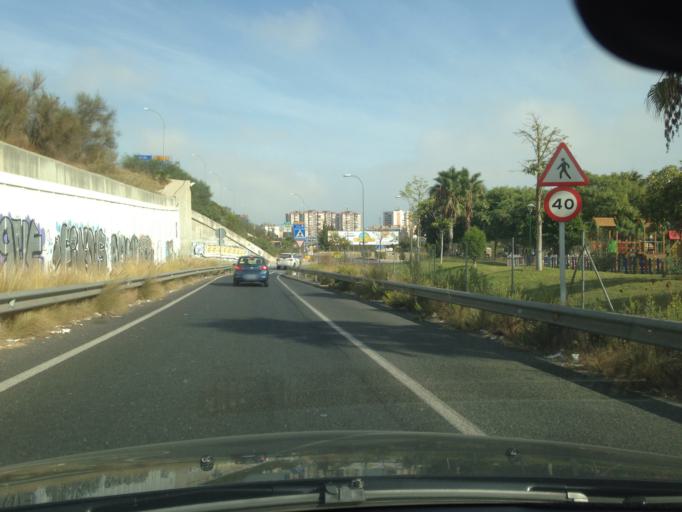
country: ES
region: Andalusia
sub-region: Provincia de Malaga
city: Malaga
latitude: 36.7124
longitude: -4.4641
